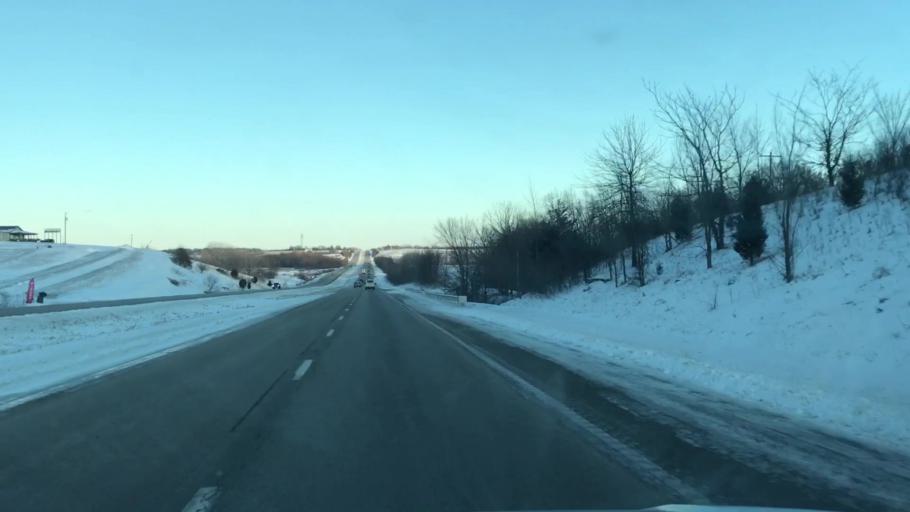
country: US
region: Missouri
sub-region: Clinton County
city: Gower
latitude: 39.7474
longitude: -94.6770
